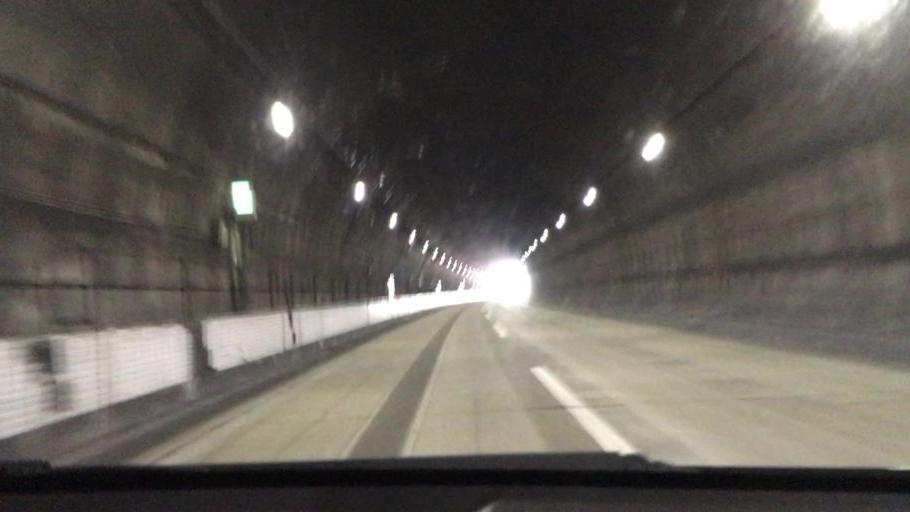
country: JP
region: Yamaguchi
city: Hofu
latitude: 34.0561
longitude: 131.6204
